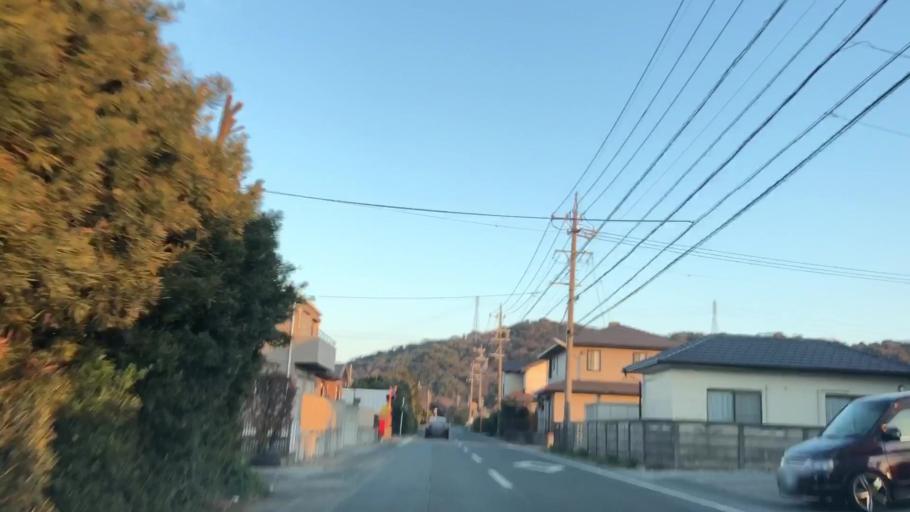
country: JP
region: Aichi
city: Toyohama
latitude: 34.6058
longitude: 137.0547
